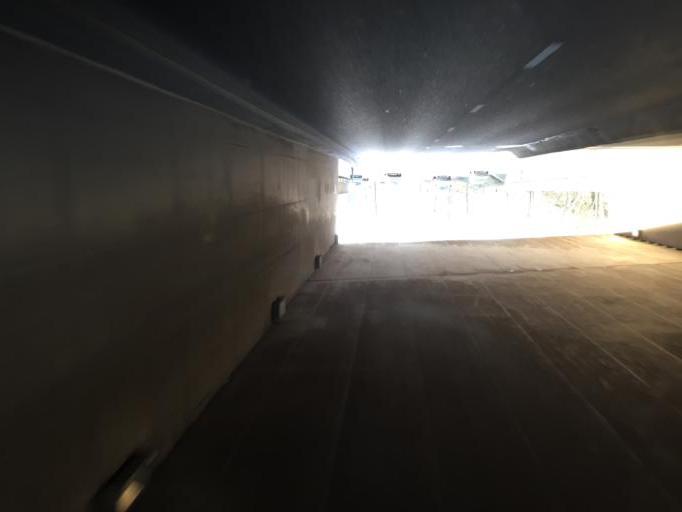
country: NL
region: North Brabant
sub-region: Gemeente 's-Hertogenbosch
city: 's-Hertogenbosch
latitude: 51.7023
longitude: 5.3037
